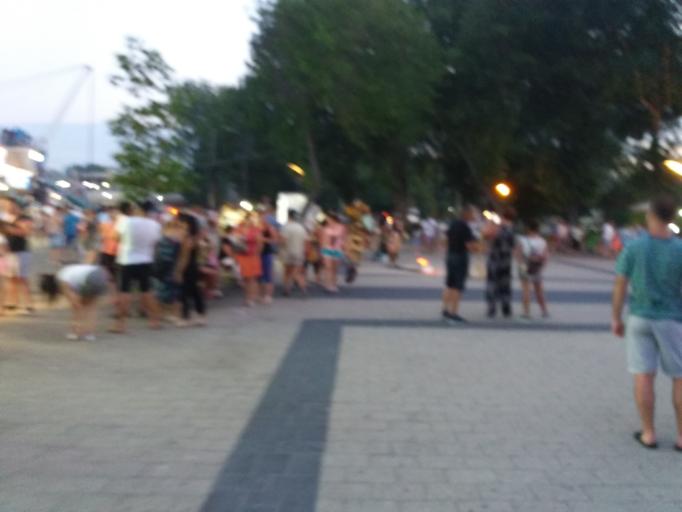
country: RO
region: Constanta
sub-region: Municipiul Constanta
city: Palazu Mare
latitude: 44.2194
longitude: 28.6321
